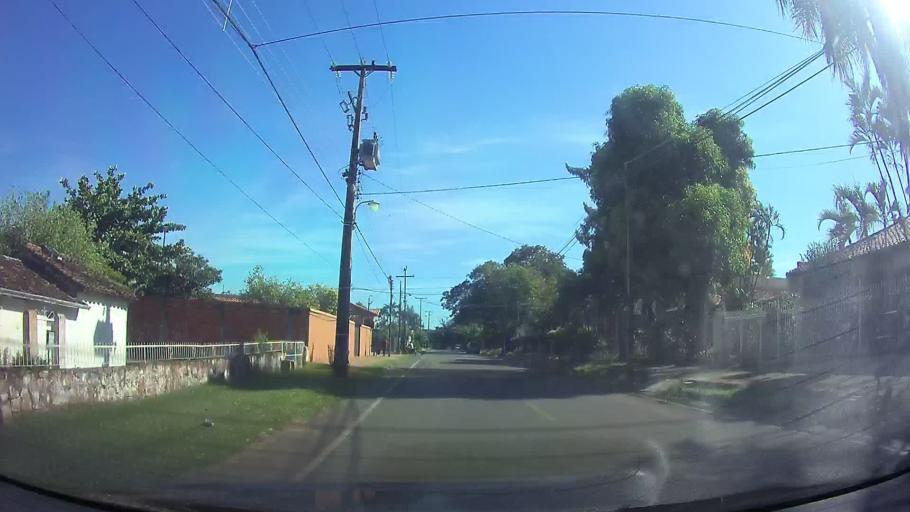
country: PY
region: Central
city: Fernando de la Mora
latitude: -25.2676
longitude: -57.5150
